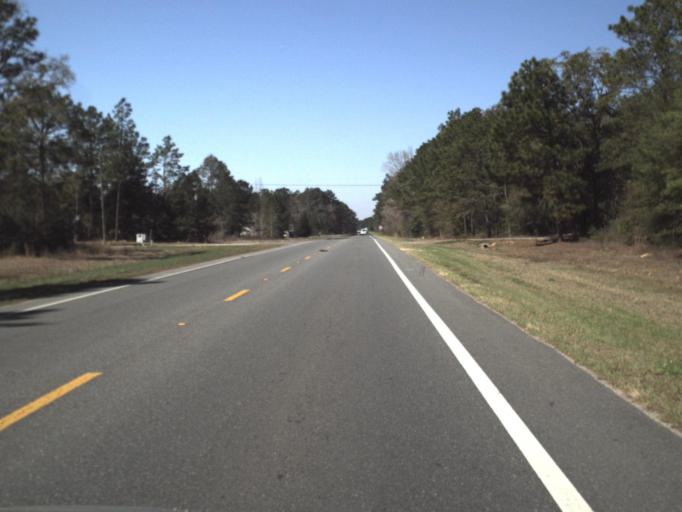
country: US
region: Florida
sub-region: Jackson County
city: Marianna
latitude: 30.7414
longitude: -85.1492
